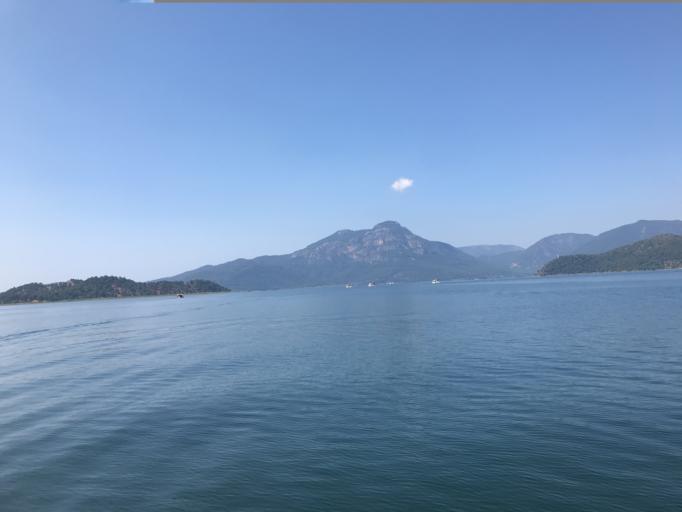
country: TR
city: Dalyan
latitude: 36.9135
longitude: 28.6555
